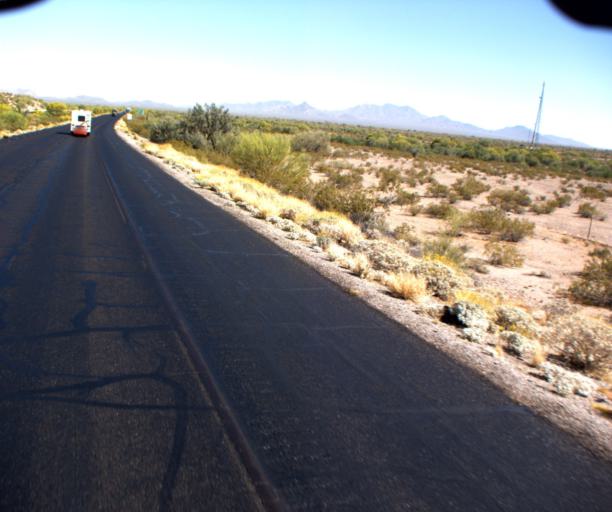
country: US
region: Arizona
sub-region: Pinal County
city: Maricopa
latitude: 32.8485
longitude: -112.3118
